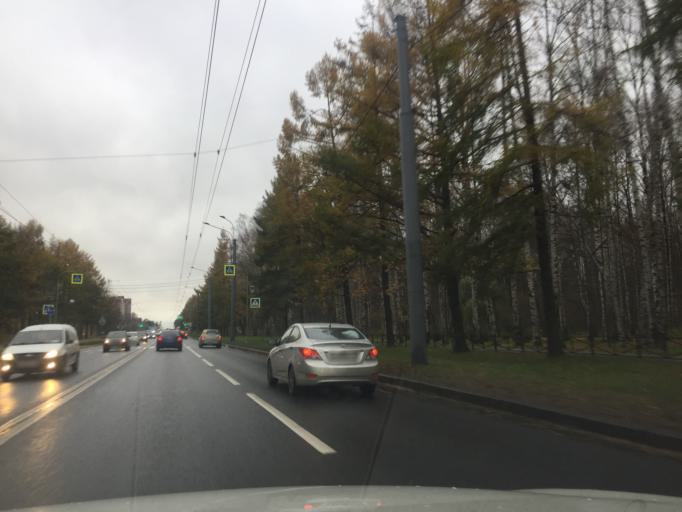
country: RU
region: St.-Petersburg
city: Sosnovka
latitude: 60.0166
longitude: 30.3617
